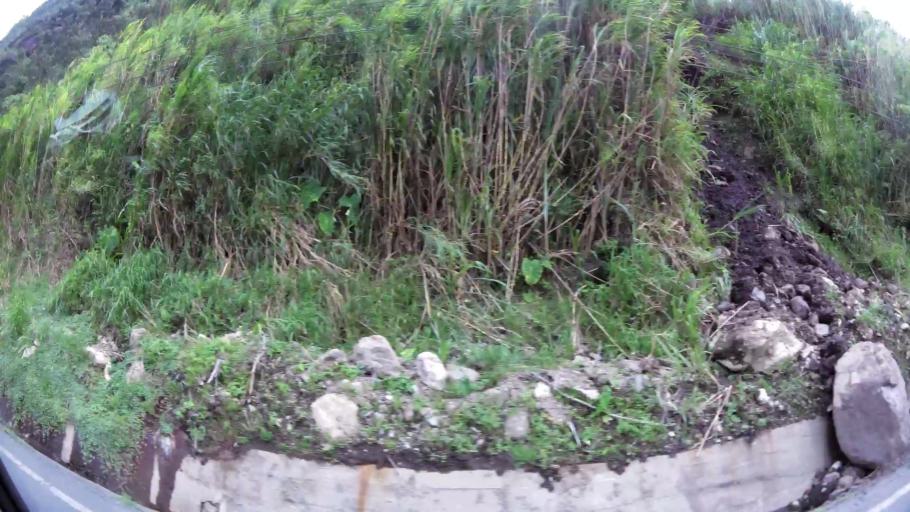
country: EC
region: Tungurahua
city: Banos
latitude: -1.3991
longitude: -78.3816
